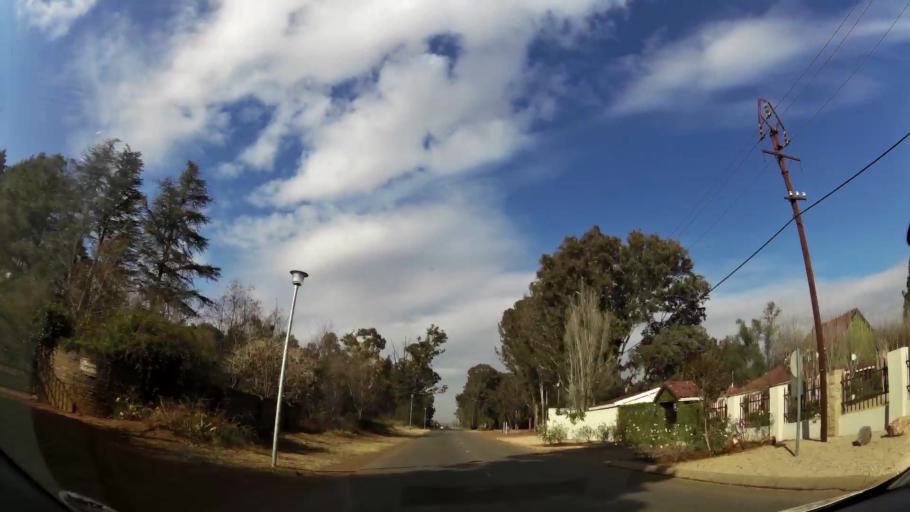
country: ZA
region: Gauteng
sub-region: Sedibeng District Municipality
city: Meyerton
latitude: -26.5447
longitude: 28.0615
